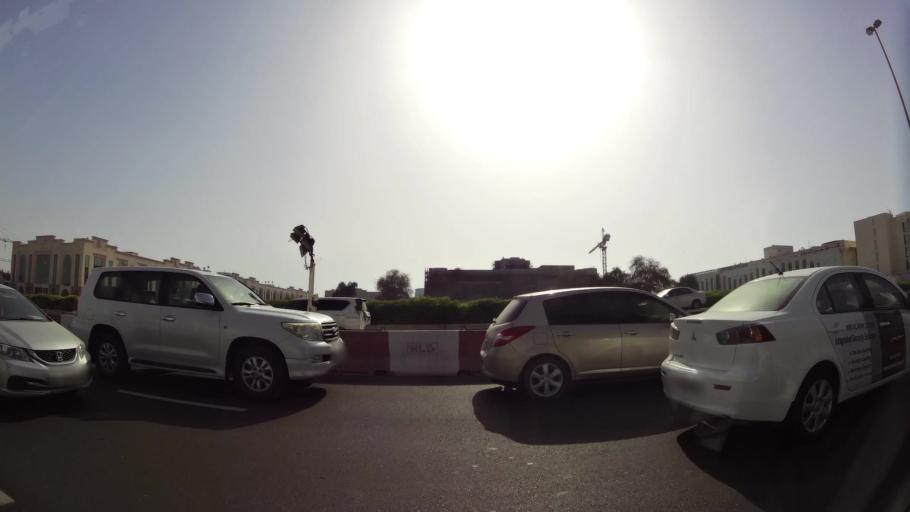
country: AE
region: Ash Shariqah
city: Sharjah
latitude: 25.2467
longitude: 55.3446
